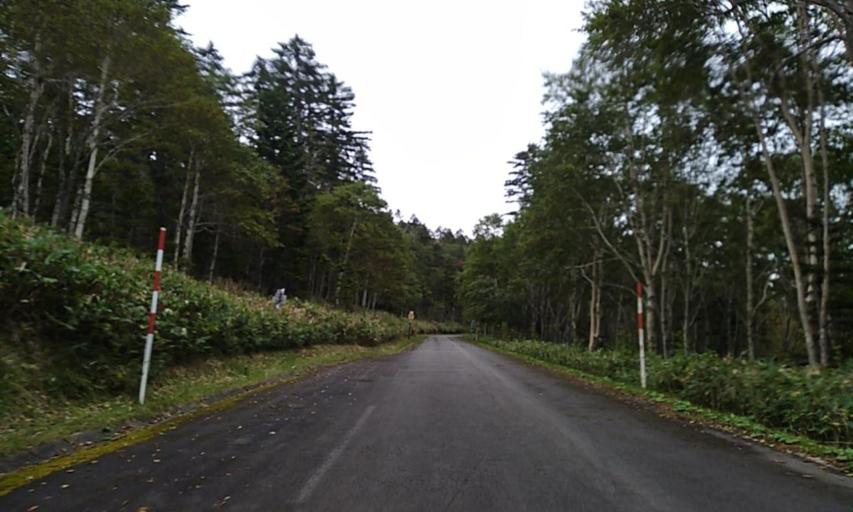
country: JP
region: Hokkaido
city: Bihoro
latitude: 43.5752
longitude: 144.2261
